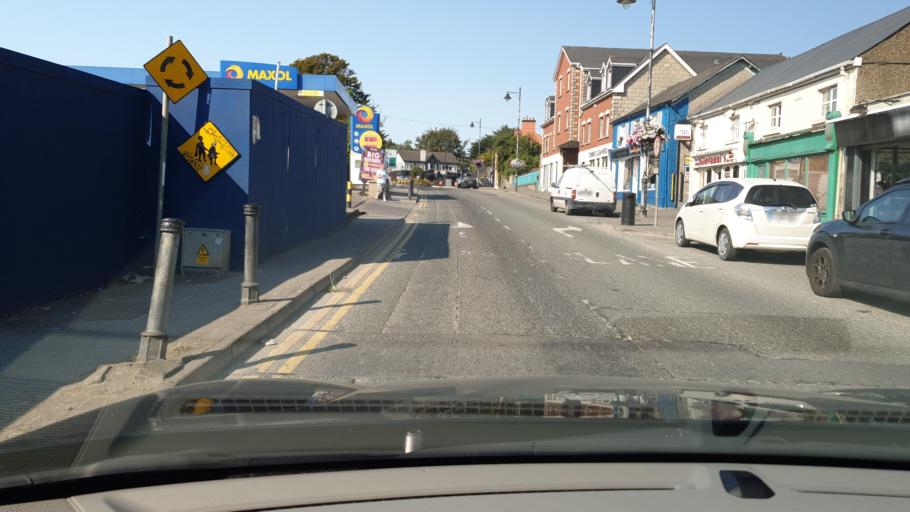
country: IE
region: Leinster
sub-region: An Mhi
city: Navan
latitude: 53.6574
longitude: -6.6800
